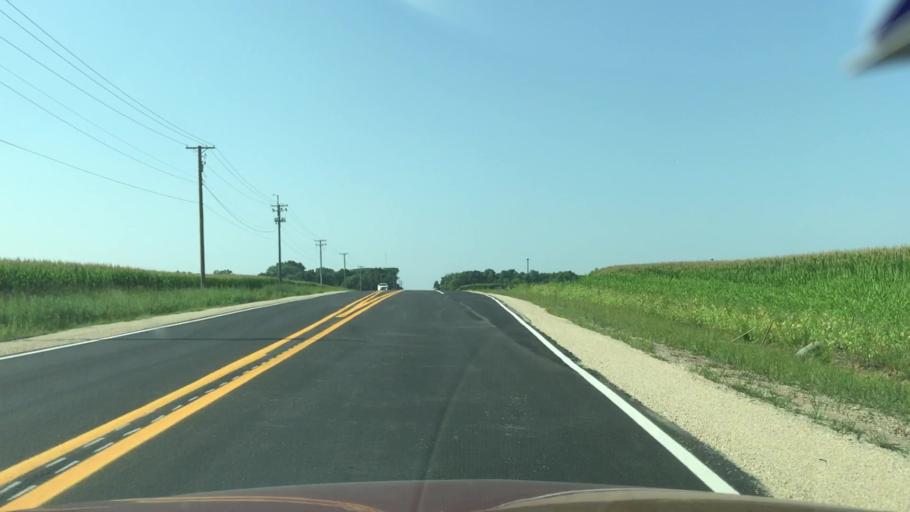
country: US
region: Illinois
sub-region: Winnebago County
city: Cherry Valley
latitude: 42.2348
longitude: -88.9796
